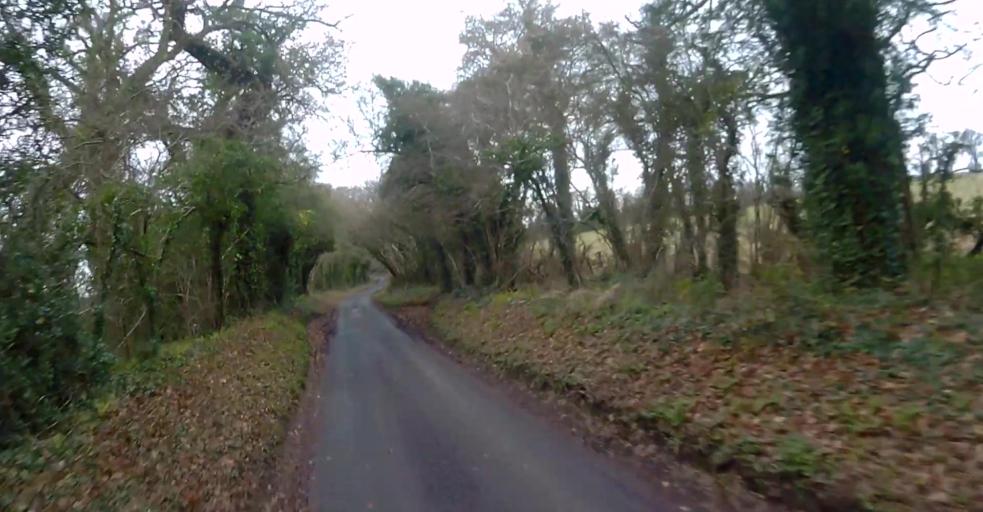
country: GB
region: England
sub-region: Hampshire
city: Overton
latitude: 51.2188
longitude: -1.2210
